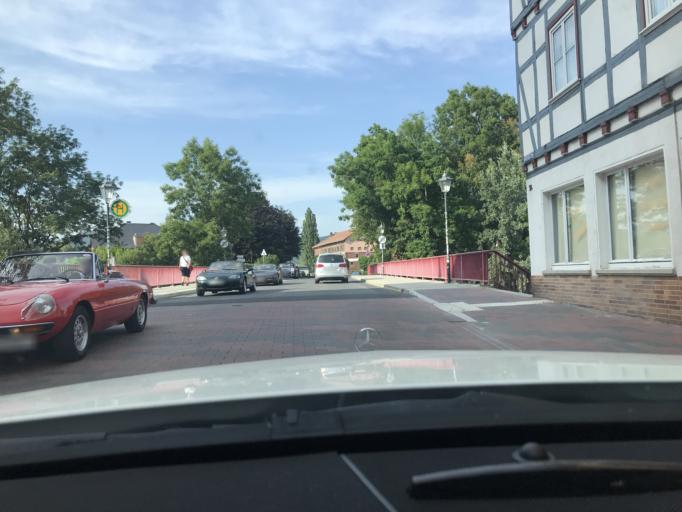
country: DE
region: Hesse
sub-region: Regierungsbezirk Kassel
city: Eschwege
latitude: 51.1908
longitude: 10.0568
